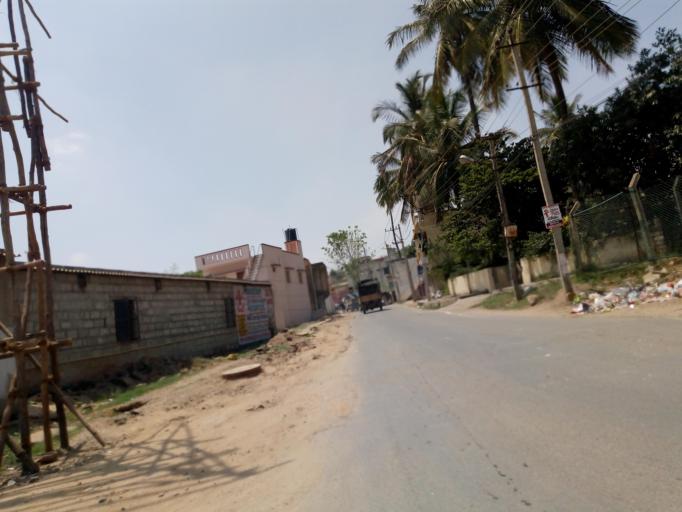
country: IN
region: Karnataka
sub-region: Bangalore Urban
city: Bangalore
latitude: 12.8906
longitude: 77.6562
